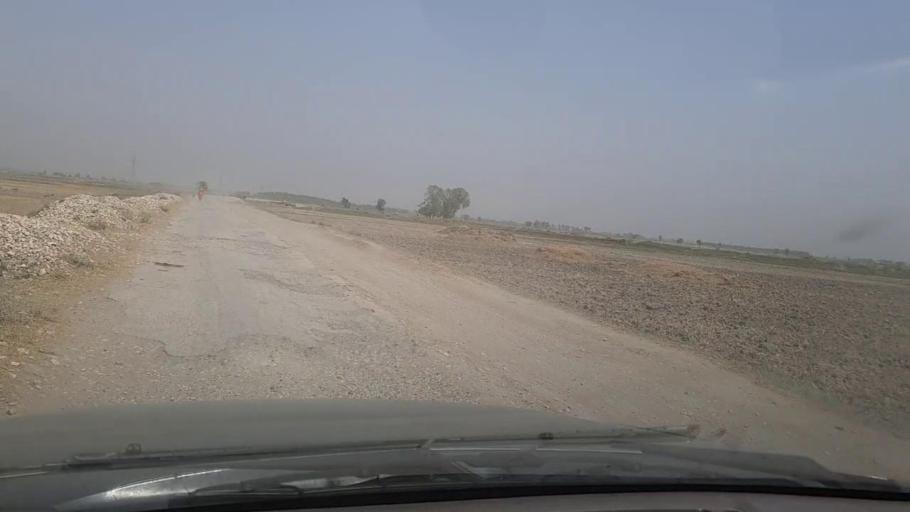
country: PK
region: Sindh
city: Madeji
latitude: 27.8074
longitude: 68.3990
